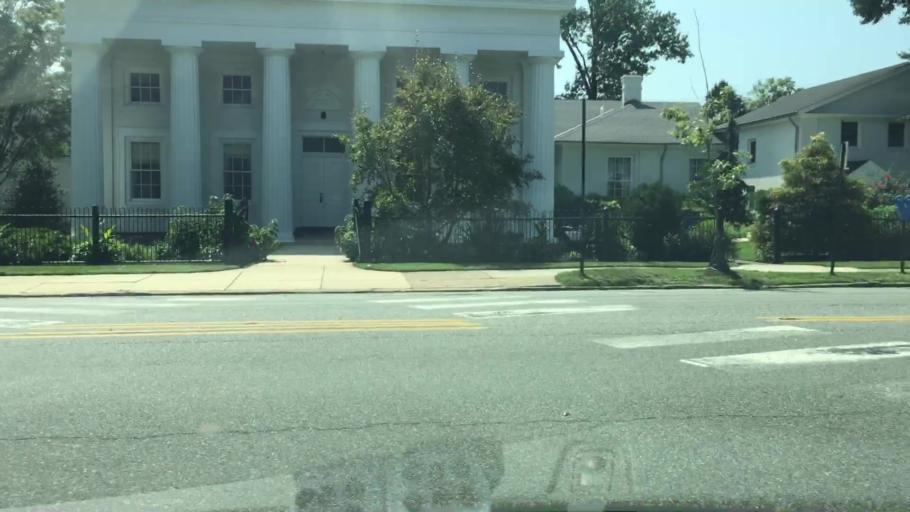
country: US
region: Pennsylvania
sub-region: Delaware County
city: Media
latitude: 39.9170
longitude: -75.3888
